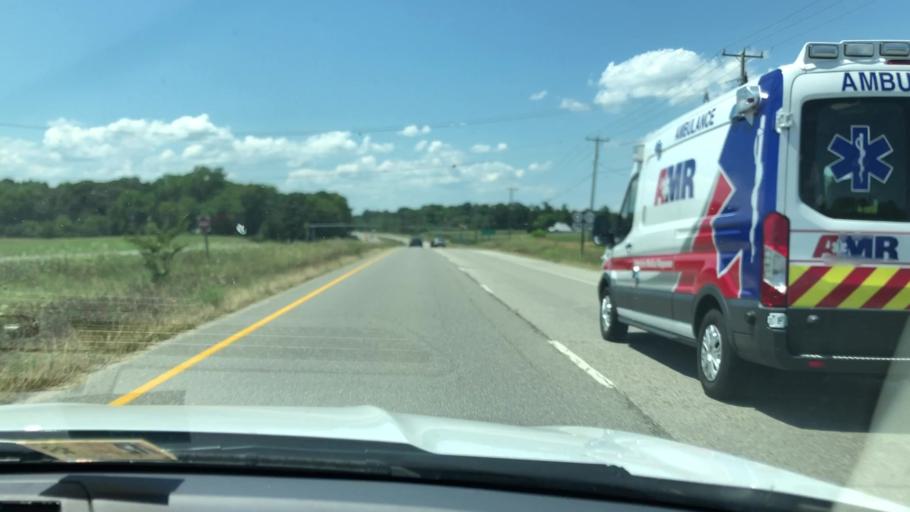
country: US
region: Virginia
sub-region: Middlesex County
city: Saluda
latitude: 37.5911
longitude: -76.4958
